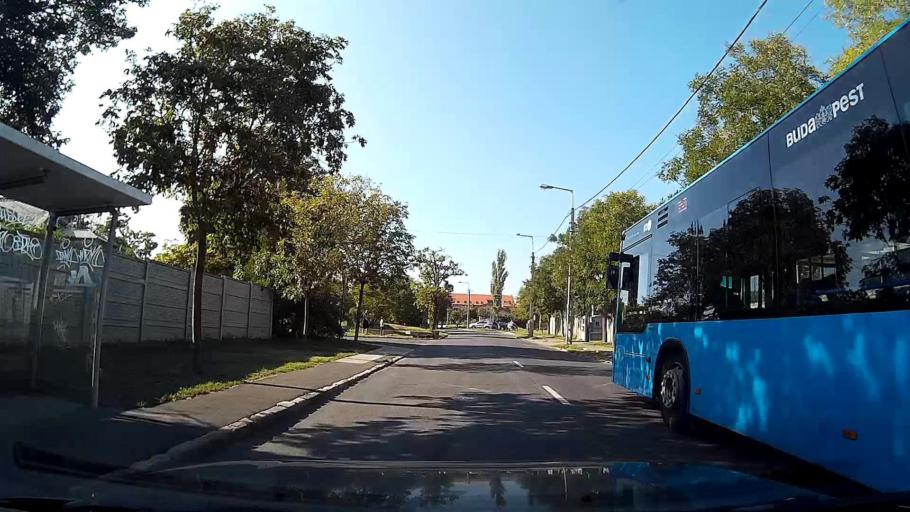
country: HU
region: Budapest
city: Budapest XXII. keruelet
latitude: 47.4147
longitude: 19.0158
